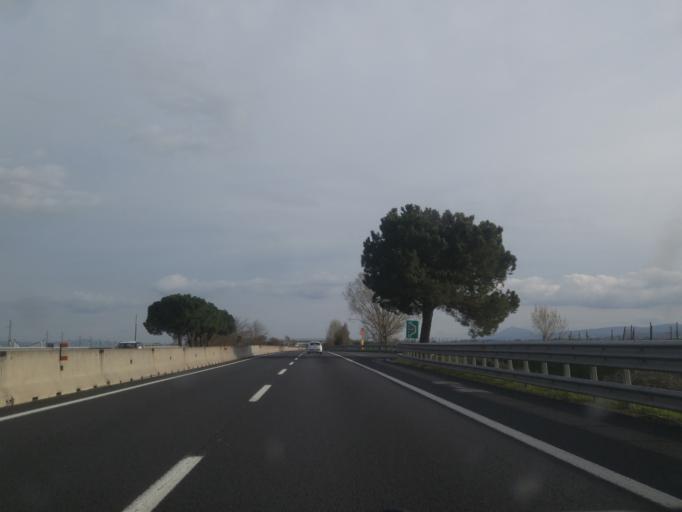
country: IT
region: Tuscany
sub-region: Provincia di Siena
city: Bettolle
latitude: 43.1798
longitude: 11.8303
